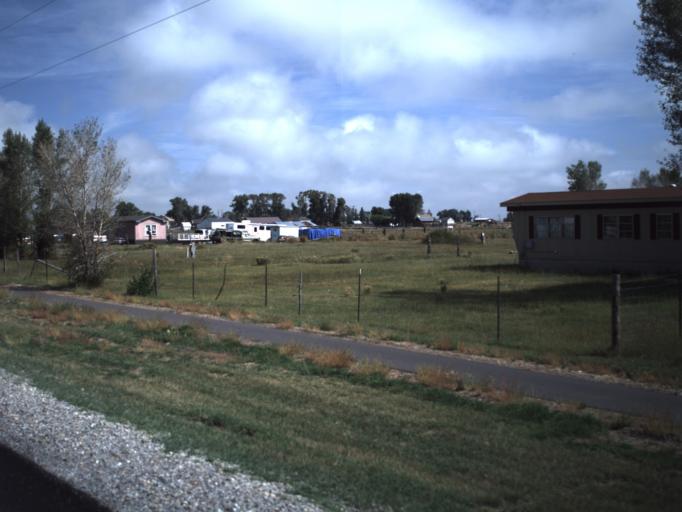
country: US
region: Utah
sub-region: Rich County
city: Randolph
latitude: 41.6594
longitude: -111.1849
